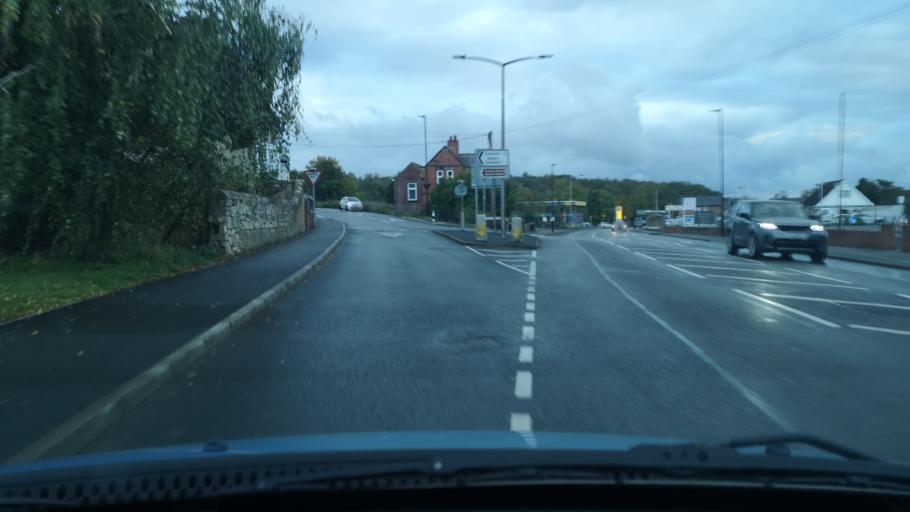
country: GB
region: England
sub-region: Doncaster
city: Askern
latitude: 53.6176
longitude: -1.1532
